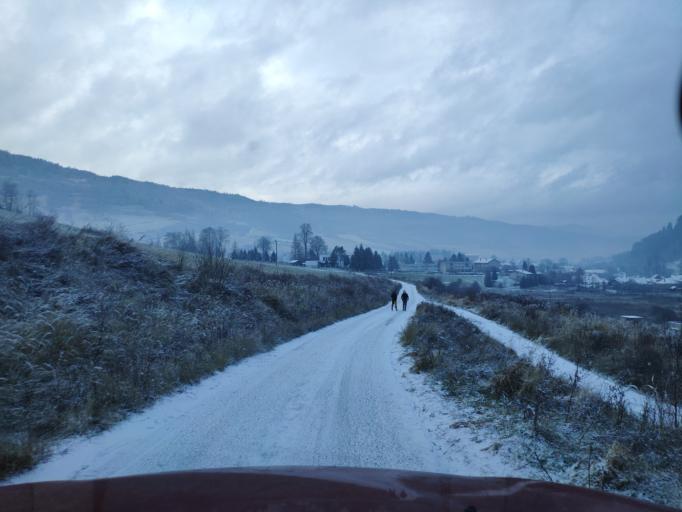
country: SK
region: Kosicky
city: Spisska Nova Ves
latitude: 48.8394
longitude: 20.6105
